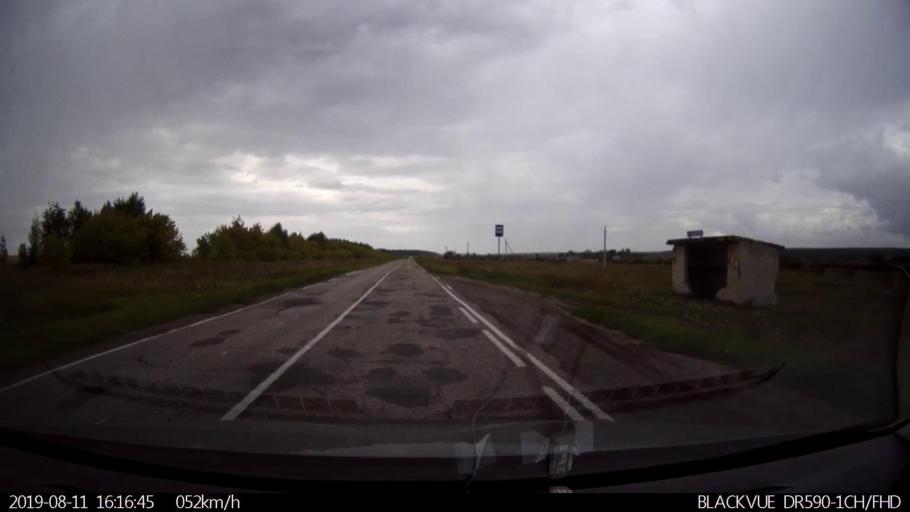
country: RU
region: Ulyanovsk
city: Mayna
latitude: 54.0434
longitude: 47.6198
